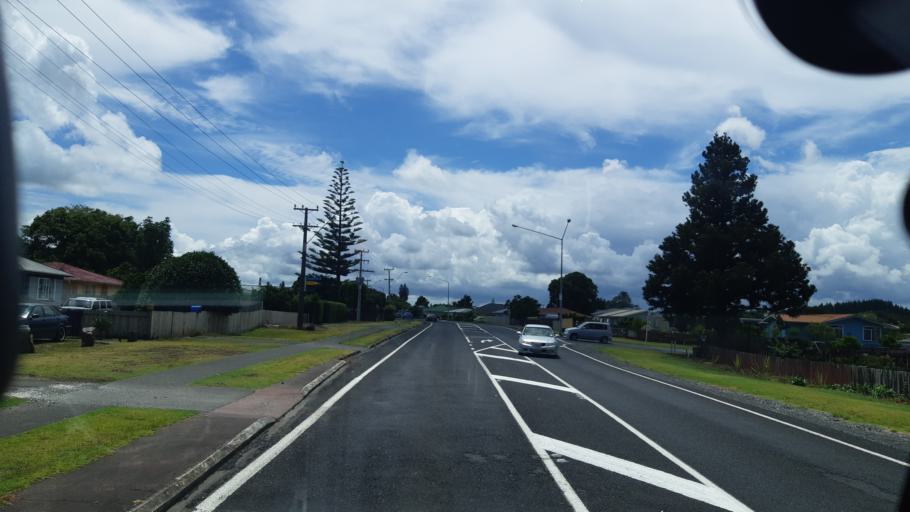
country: NZ
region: Northland
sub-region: Far North District
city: Moerewa
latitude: -35.3895
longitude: 174.0077
